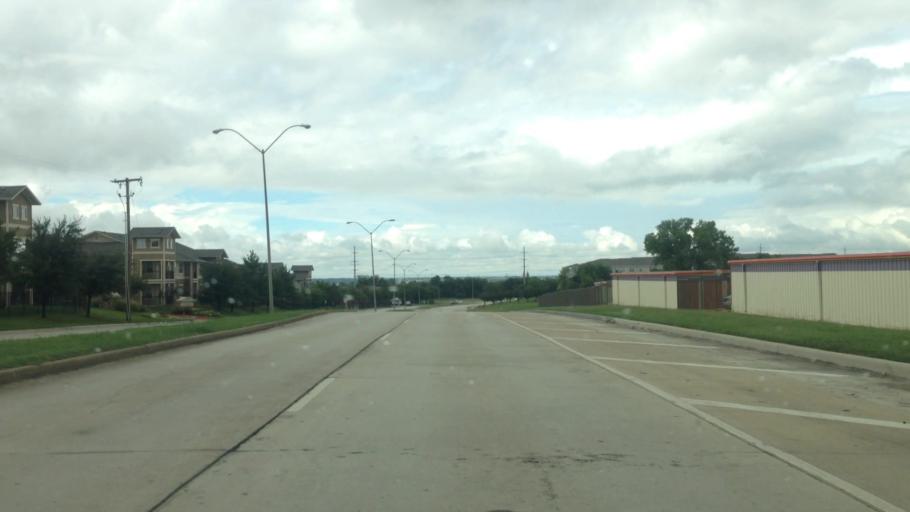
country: US
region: Texas
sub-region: Tarrant County
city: Benbrook
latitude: 32.6469
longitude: -97.4096
